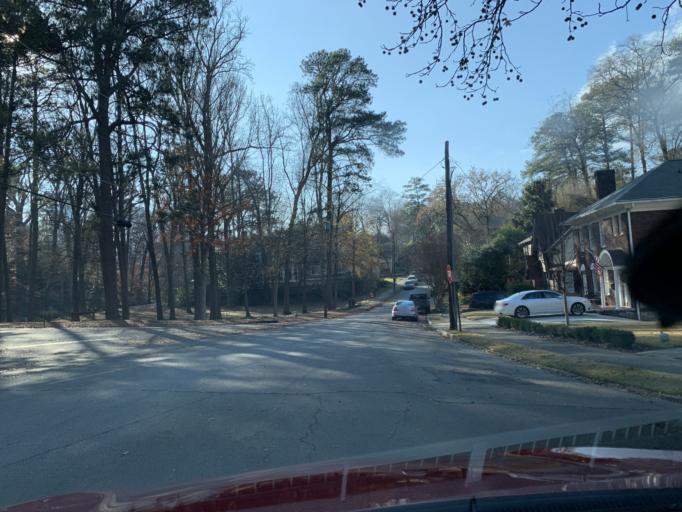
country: US
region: Georgia
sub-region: DeKalb County
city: Druid Hills
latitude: 33.7962
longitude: -84.3747
